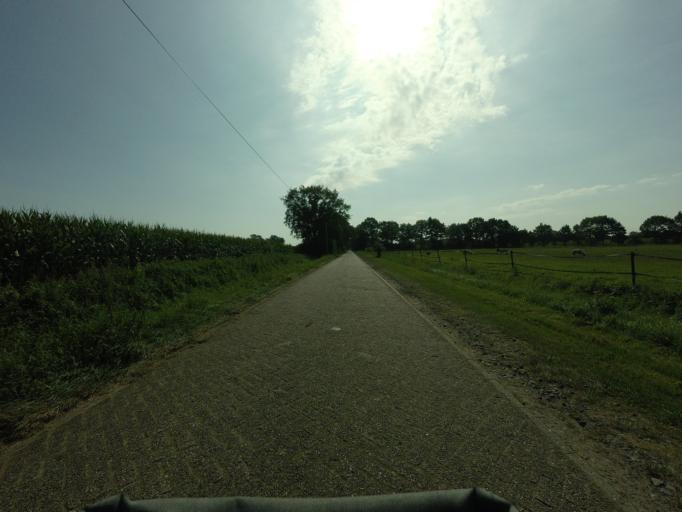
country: DE
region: Lower Saxony
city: Wilsum
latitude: 52.5605
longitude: 6.8310
